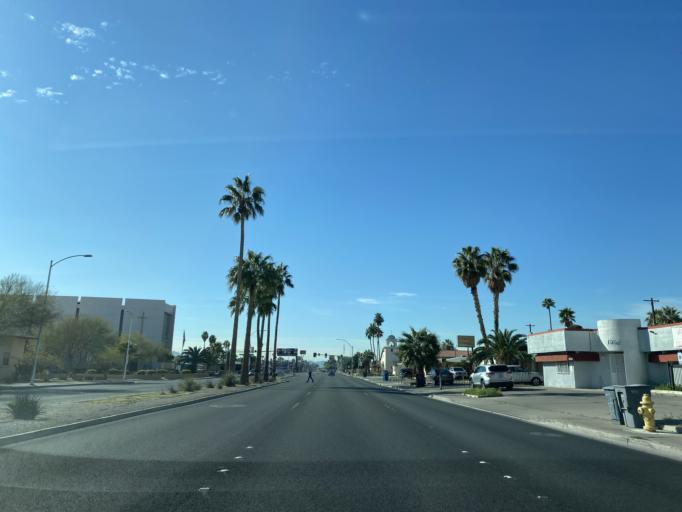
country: US
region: Nevada
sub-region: Clark County
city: Las Vegas
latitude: 36.1495
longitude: -115.1371
